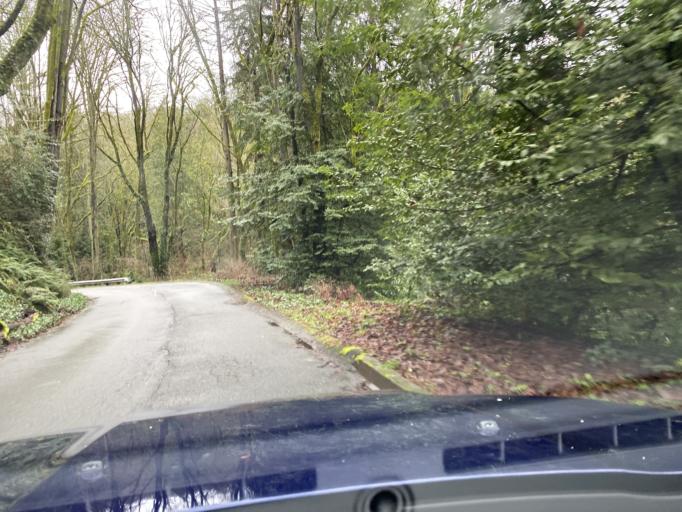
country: US
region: Washington
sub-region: King County
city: Seattle
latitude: 47.6374
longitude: -122.3097
